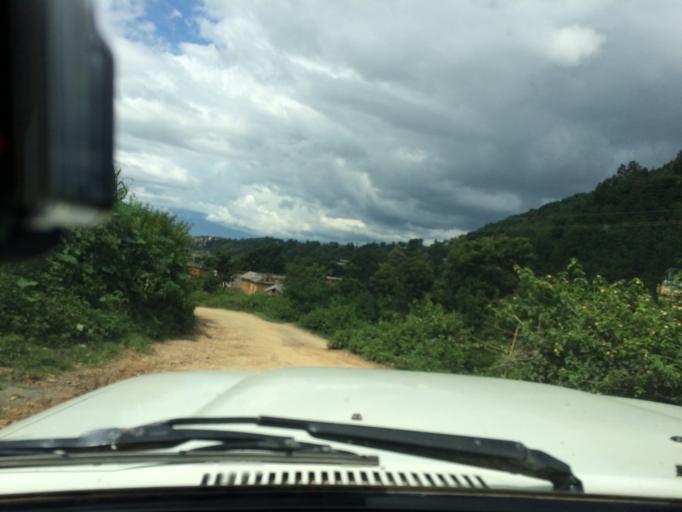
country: NP
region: Central Region
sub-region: Bagmati Zone
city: Patan
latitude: 27.5839
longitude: 85.3091
